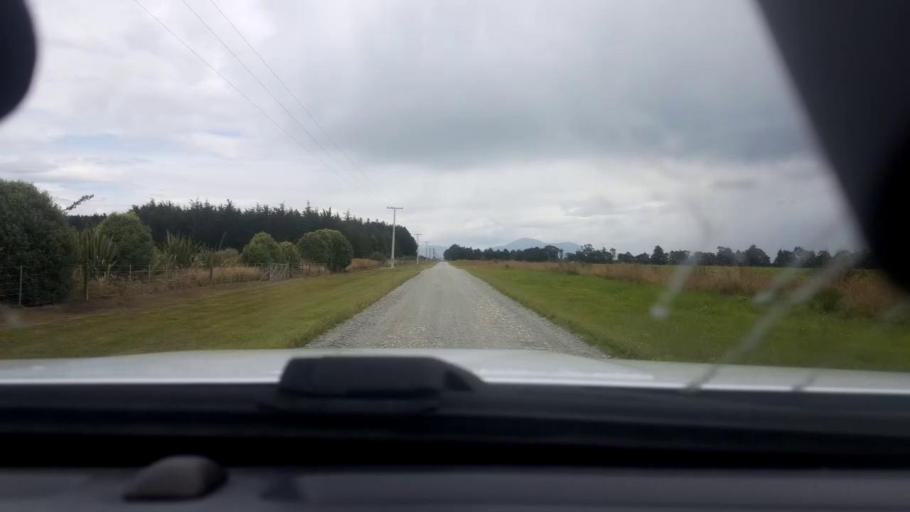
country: NZ
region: Canterbury
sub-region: Timaru District
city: Timaru
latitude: -44.1629
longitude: 171.4066
